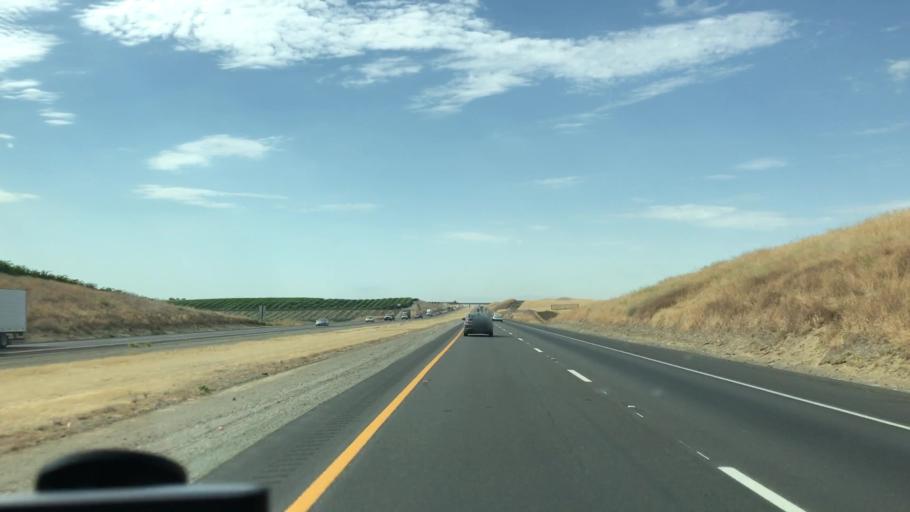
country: US
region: California
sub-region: Stanislaus County
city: Patterson
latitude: 37.3660
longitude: -121.1234
